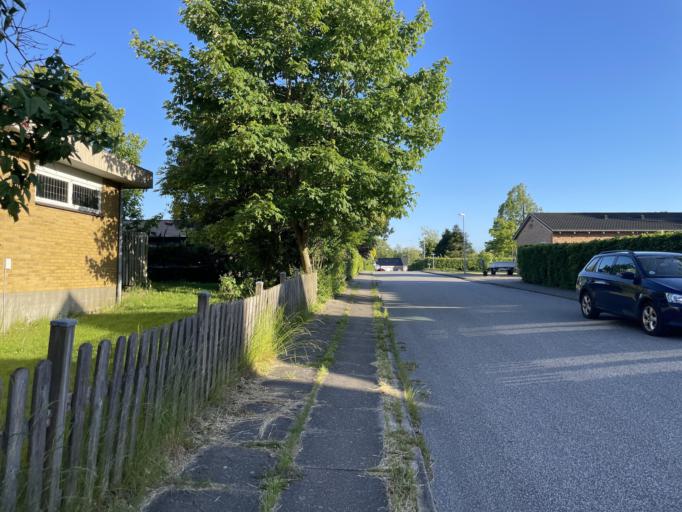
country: DK
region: South Denmark
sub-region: Vejle Kommune
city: Jelling
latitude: 55.7570
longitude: 9.4296
